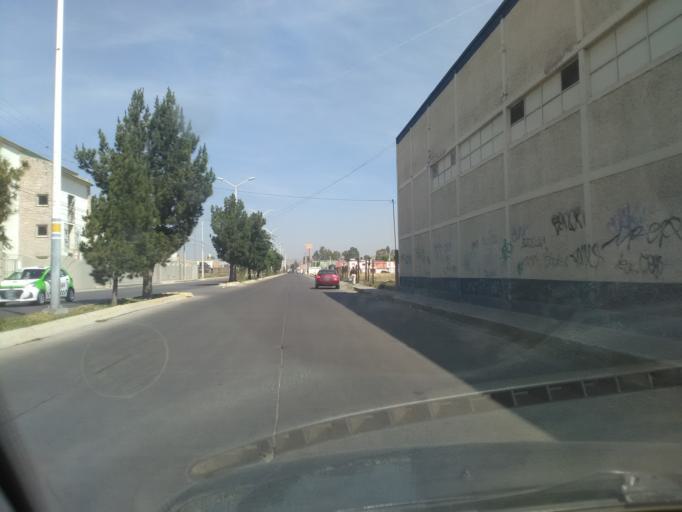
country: MX
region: Durango
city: Victoria de Durango
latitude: 24.0475
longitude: -104.6242
